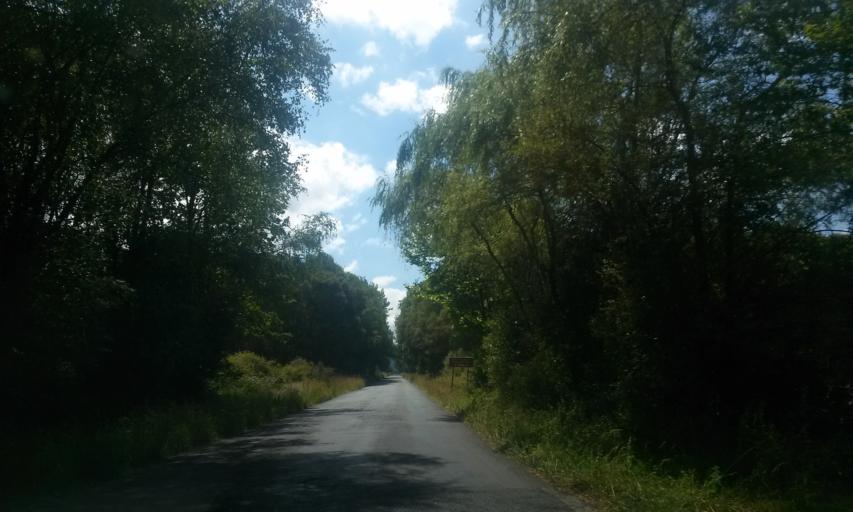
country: ES
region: Galicia
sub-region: Provincia de Lugo
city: Rabade
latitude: 43.1171
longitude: -7.6366
